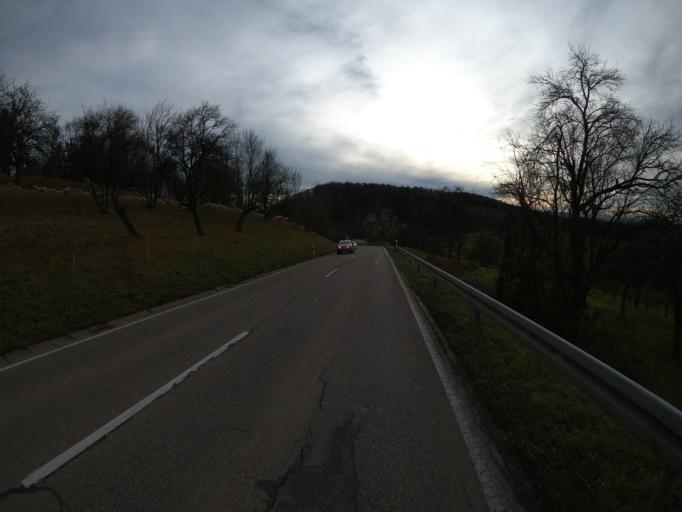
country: DE
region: Baden-Wuerttemberg
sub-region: Regierungsbezirk Stuttgart
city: Ottenbach
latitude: 48.7360
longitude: 9.7180
